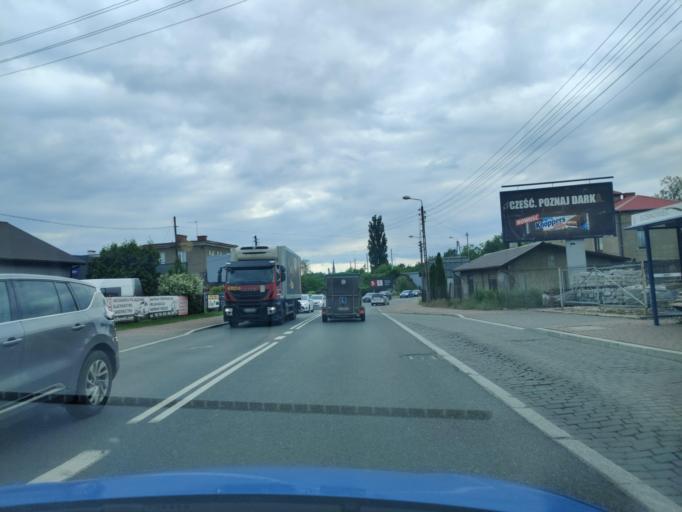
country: PL
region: Silesian Voivodeship
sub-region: Myslowice
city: Myslowice
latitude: 50.2381
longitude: 19.1562
